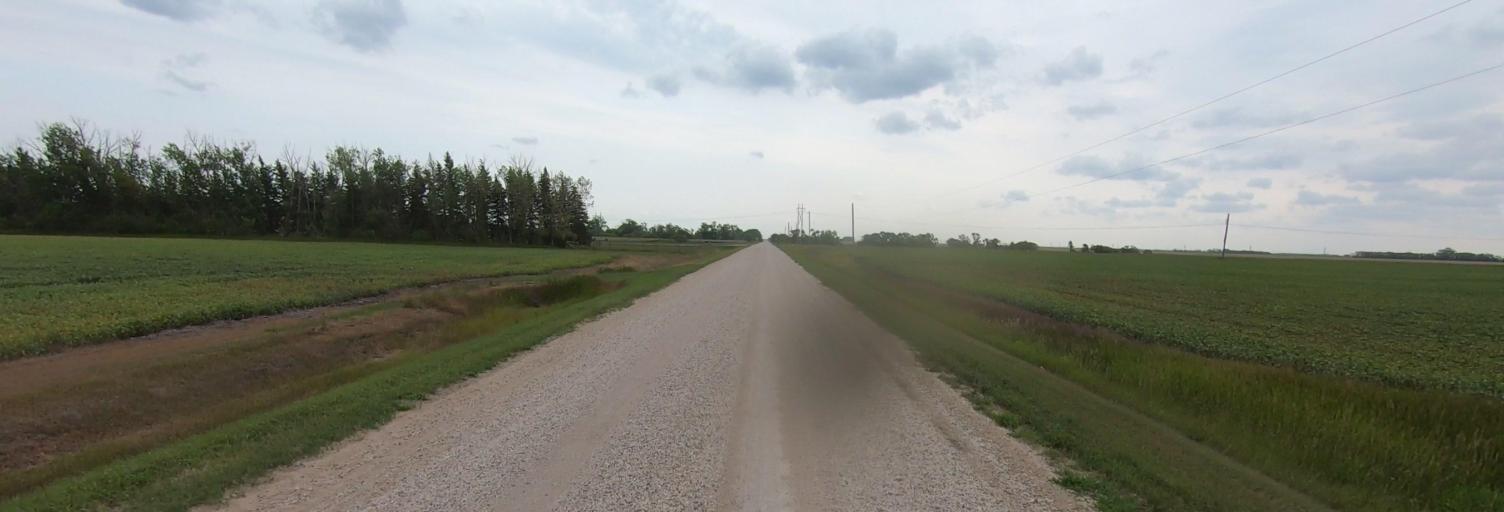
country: CA
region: Manitoba
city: Headingley
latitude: 49.7243
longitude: -97.4081
